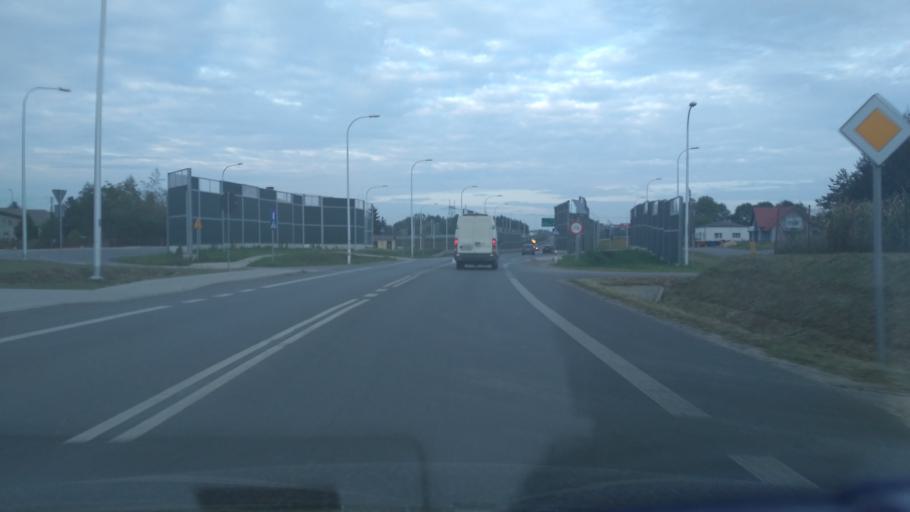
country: PL
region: Lublin Voivodeship
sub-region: Powiat lubelski
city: Jakubowice Murowane
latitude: 51.2740
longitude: 22.6469
